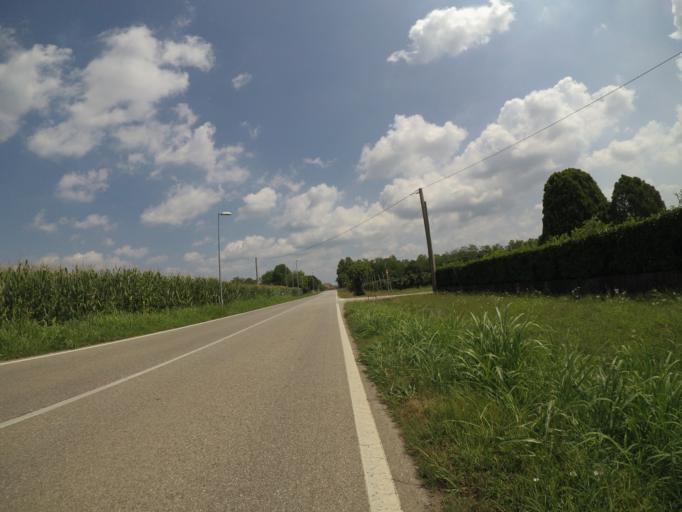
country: IT
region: Friuli Venezia Giulia
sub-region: Provincia di Udine
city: Mereto di Tomba
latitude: 46.0199
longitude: 13.0279
